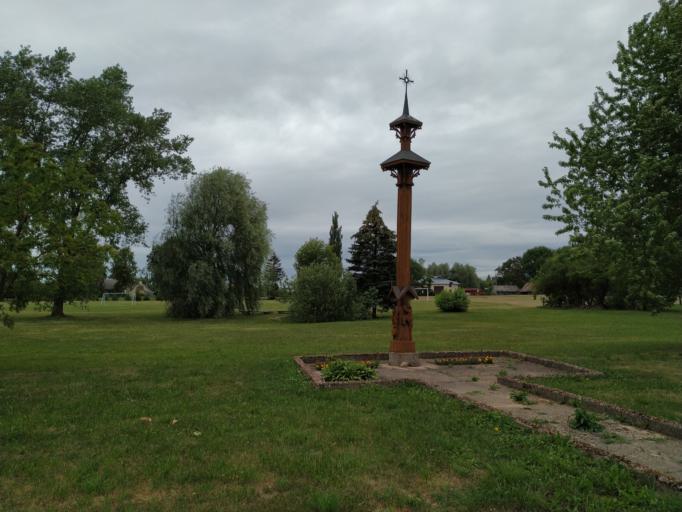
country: LT
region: Panevezys
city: Pasvalys
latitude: 56.0834
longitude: 24.5218
